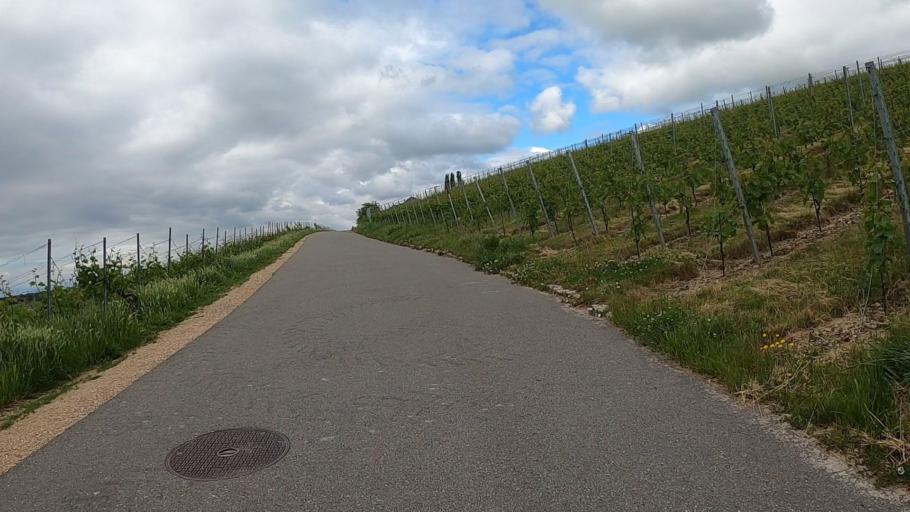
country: CH
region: Vaud
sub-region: Nyon District
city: Rolle
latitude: 46.4699
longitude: 6.3293
